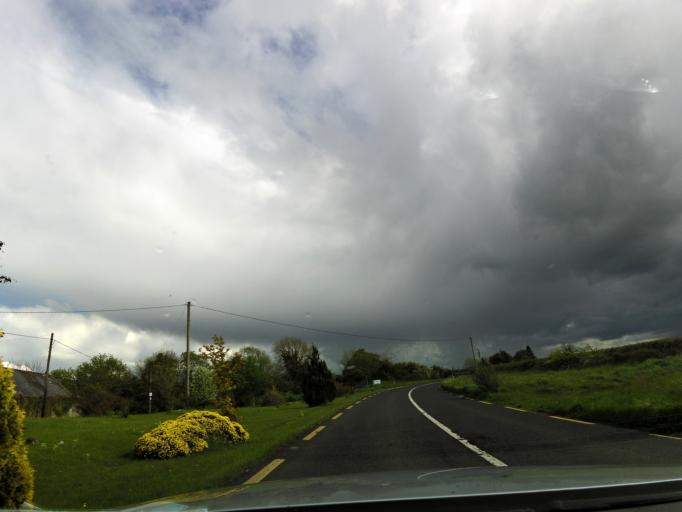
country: IE
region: Munster
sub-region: North Tipperary
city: Templemore
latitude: 52.7387
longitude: -7.8410
